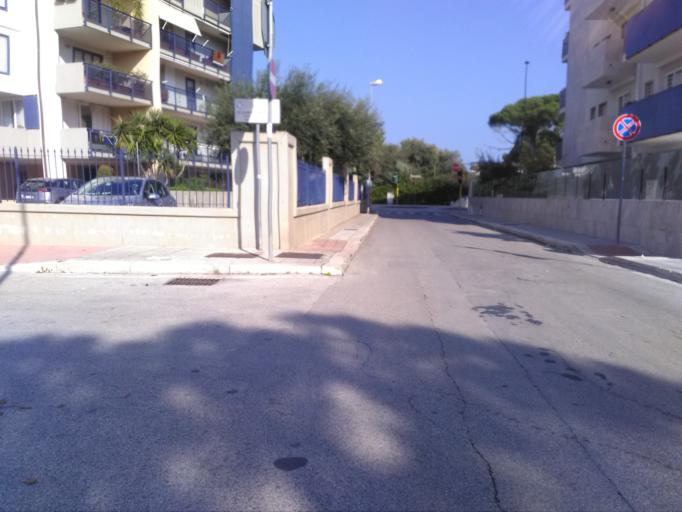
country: IT
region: Apulia
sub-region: Provincia di Bari
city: San Paolo
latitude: 41.1553
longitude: 16.7686
